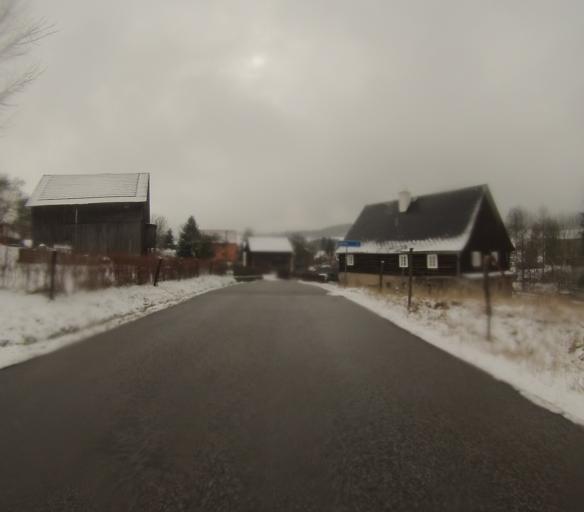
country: CZ
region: Ustecky
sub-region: Okres Decin
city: Decin
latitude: 50.7276
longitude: 14.2315
